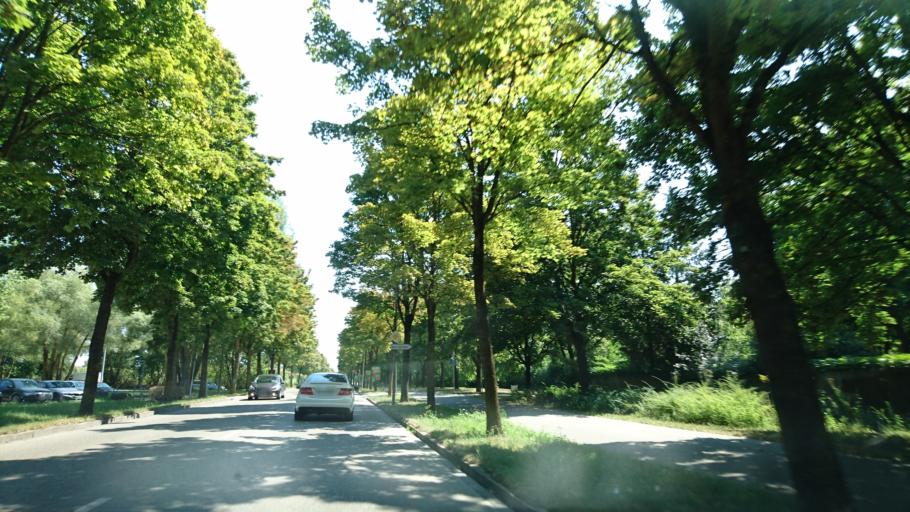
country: DE
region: Bavaria
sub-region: Swabia
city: Augsburg
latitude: 48.3696
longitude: 10.9406
